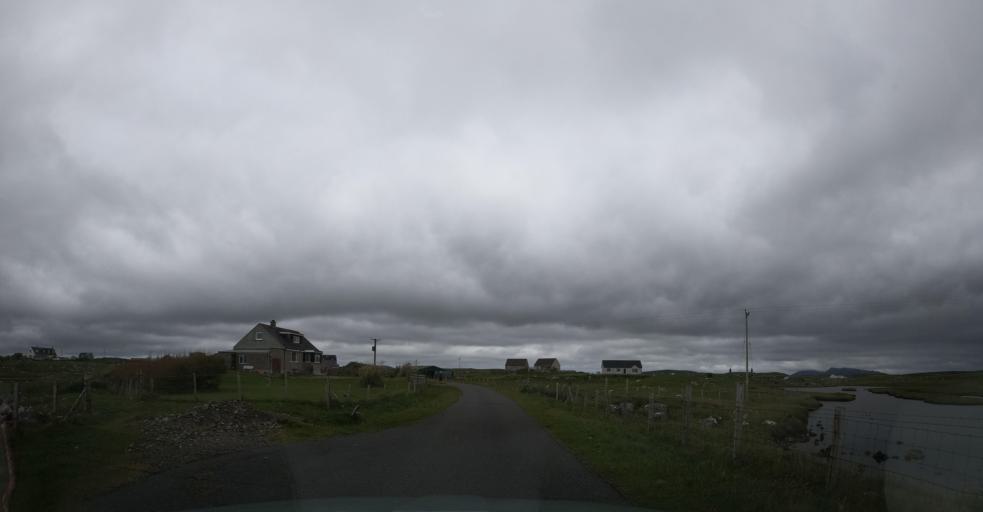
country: GB
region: Scotland
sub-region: Eilean Siar
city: Isle of North Uist
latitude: 57.5428
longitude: -7.3439
